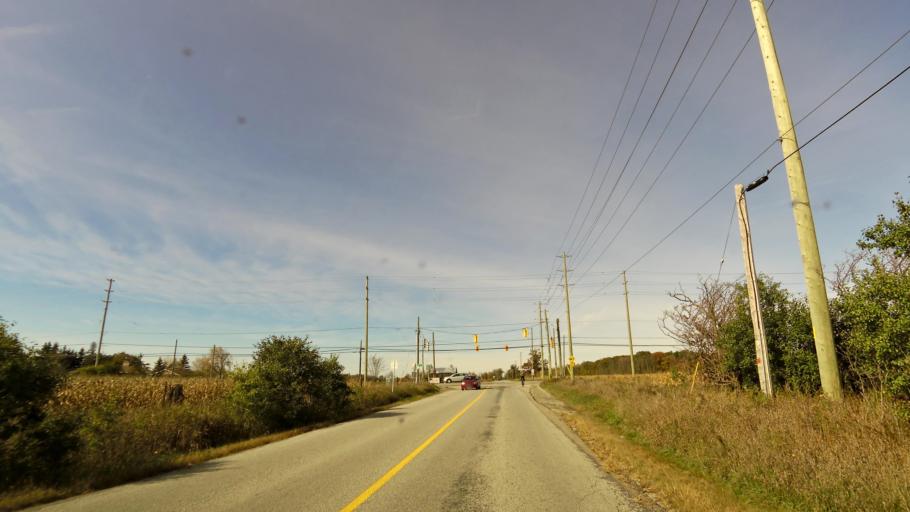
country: CA
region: Ontario
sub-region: Halton
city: Milton
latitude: 43.5254
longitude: -79.7912
